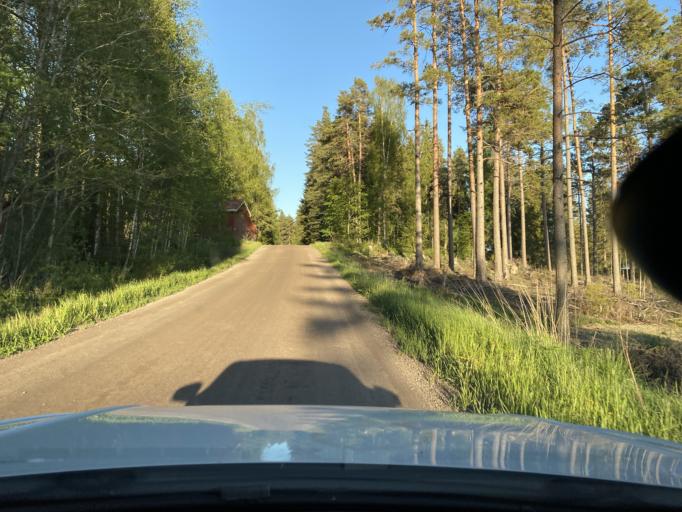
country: FI
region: Satakunta
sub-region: Rauma
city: Lappi
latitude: 61.1370
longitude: 21.9663
